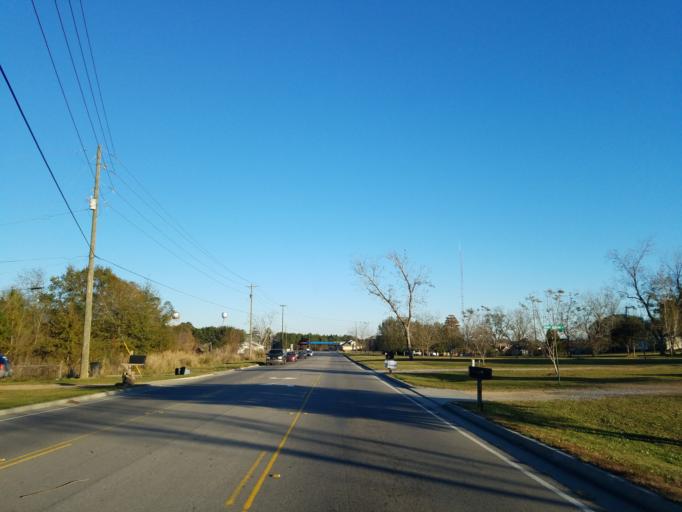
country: US
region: Mississippi
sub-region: Lamar County
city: Arnold Line
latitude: 31.3336
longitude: -89.3847
